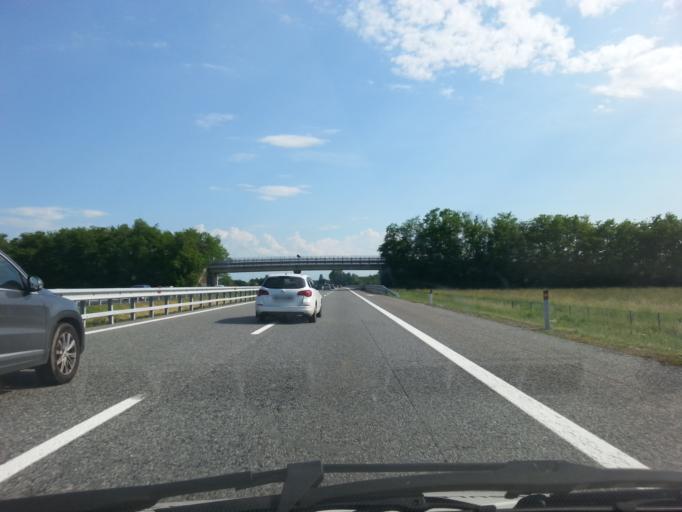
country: IT
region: Piedmont
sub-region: Provincia di Cuneo
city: Caramagna Piemonte
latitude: 44.7589
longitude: 7.7502
